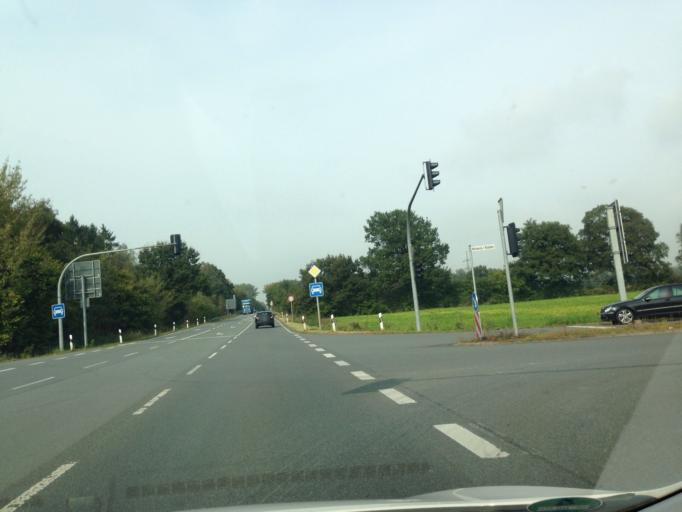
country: DE
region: North Rhine-Westphalia
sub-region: Regierungsbezirk Munster
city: Dulmen
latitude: 51.8363
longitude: 7.3185
